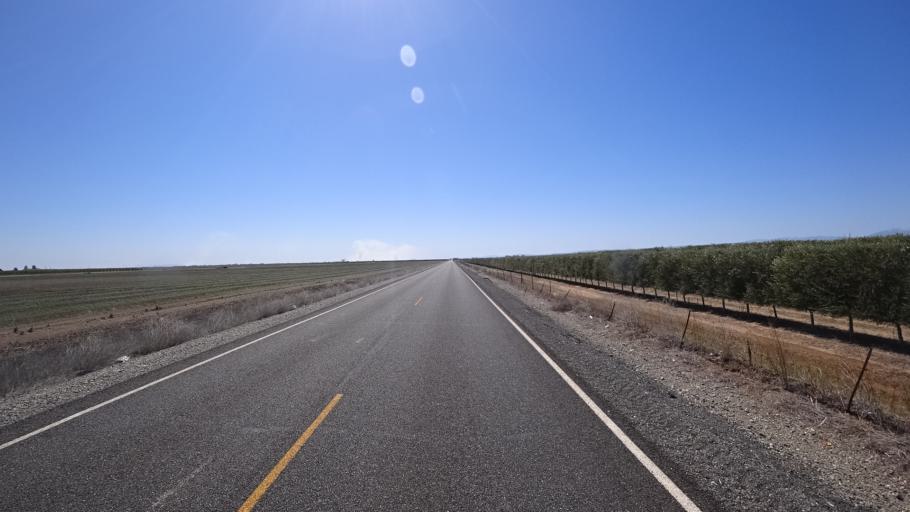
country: US
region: California
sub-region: Glenn County
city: Willows
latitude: 39.5926
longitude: -122.2498
